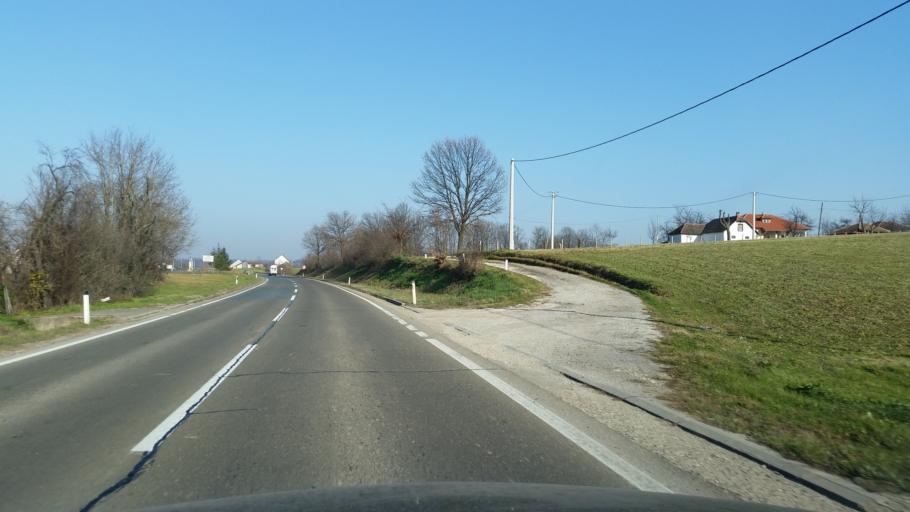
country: RS
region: Central Serbia
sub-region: Kolubarski Okrug
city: Ljig
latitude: 44.2458
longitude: 20.2817
